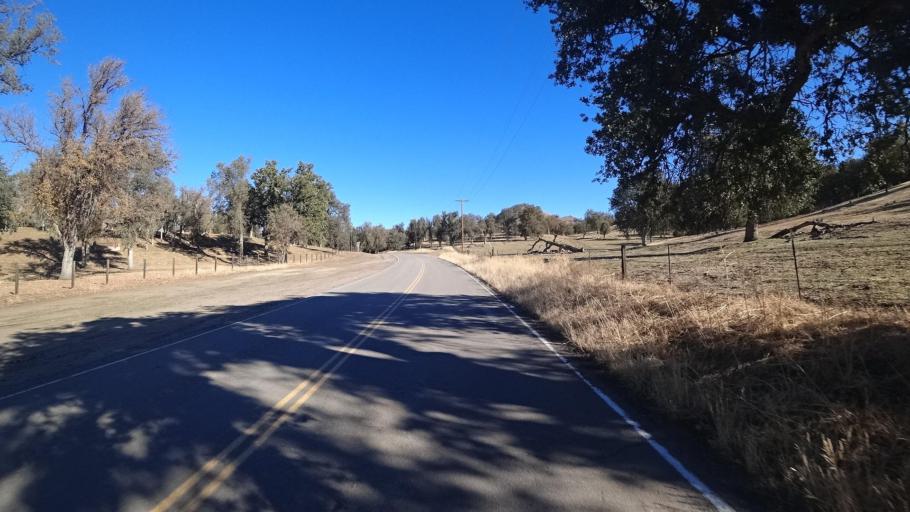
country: US
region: California
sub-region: Kern County
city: Alta Sierra
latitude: 35.7409
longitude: -118.7163
